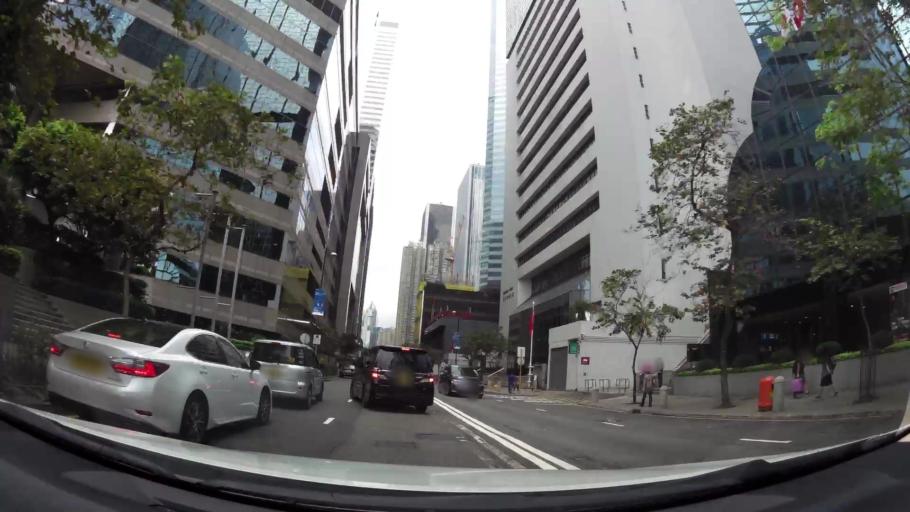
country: HK
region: Wanchai
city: Wan Chai
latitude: 22.2805
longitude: 114.1718
